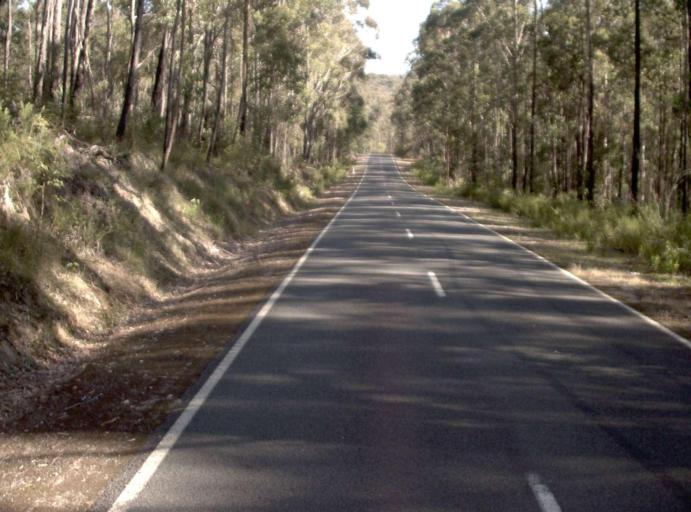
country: AU
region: Victoria
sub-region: East Gippsland
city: Lakes Entrance
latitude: -37.6567
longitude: 148.4778
